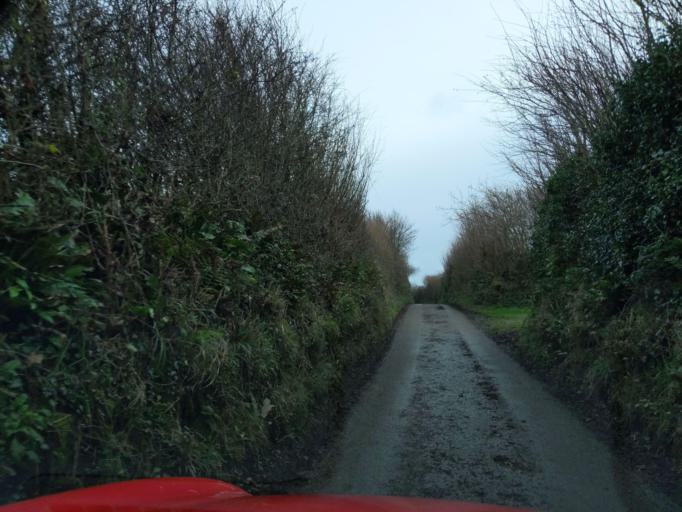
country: GB
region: England
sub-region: Cornwall
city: Duloe
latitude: 50.3532
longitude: -4.5143
